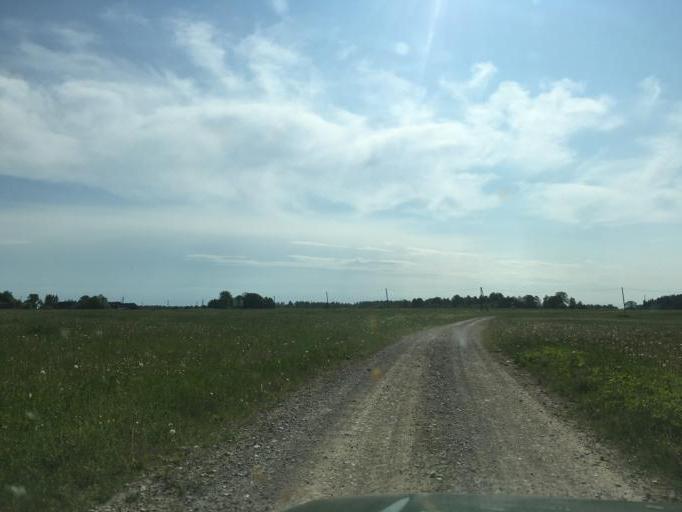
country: LV
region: Dundaga
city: Dundaga
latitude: 57.5527
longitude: 22.4675
